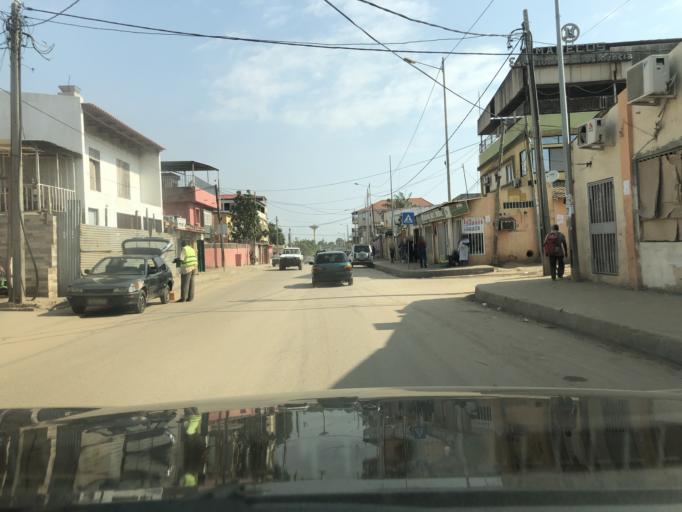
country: AO
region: Luanda
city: Luanda
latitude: -8.8487
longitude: 13.2589
